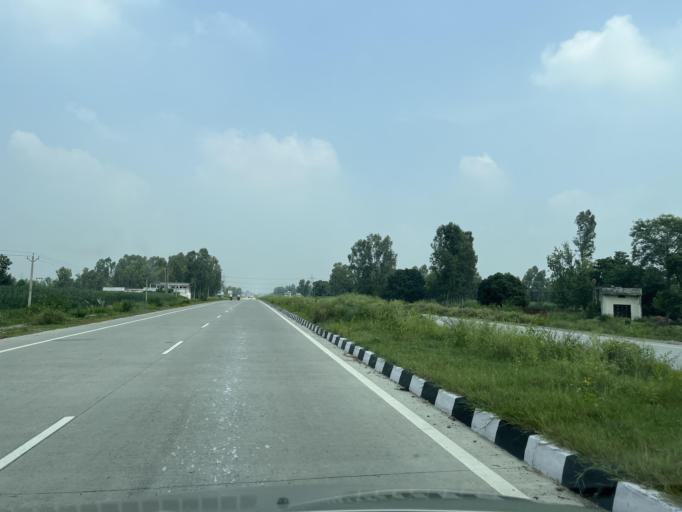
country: IN
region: Uttar Pradesh
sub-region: Bijnor
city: Najibabad
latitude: 29.5527
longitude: 78.3391
